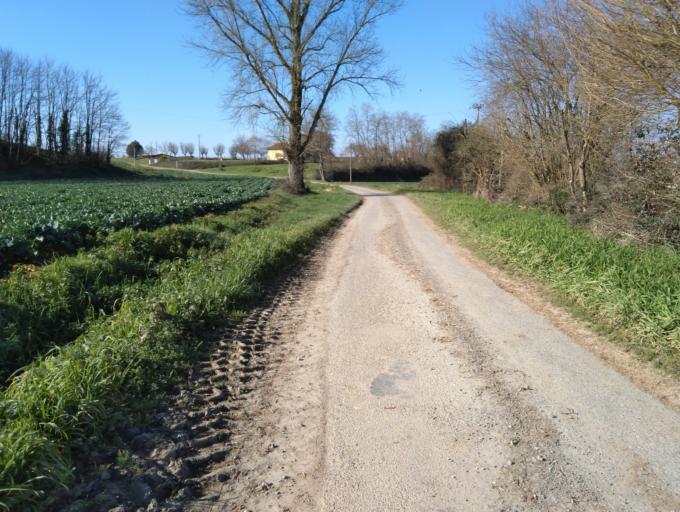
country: FR
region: Midi-Pyrenees
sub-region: Departement du Gers
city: Riscle
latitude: 43.6576
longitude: -0.0545
